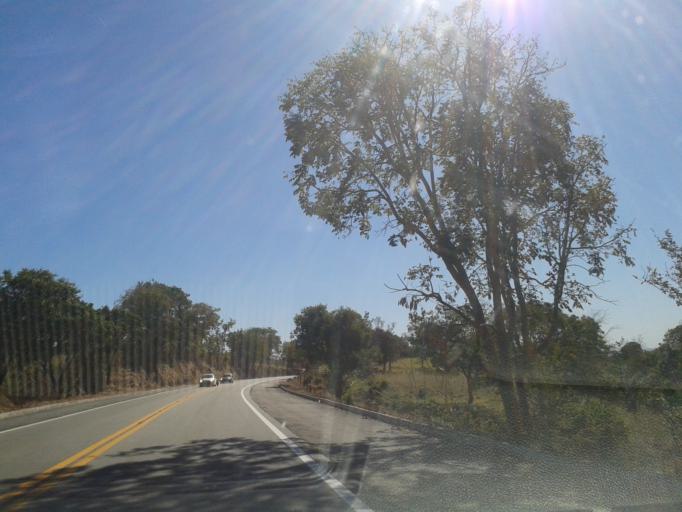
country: BR
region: Goias
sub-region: Goias
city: Goias
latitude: -15.8479
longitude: -50.1001
